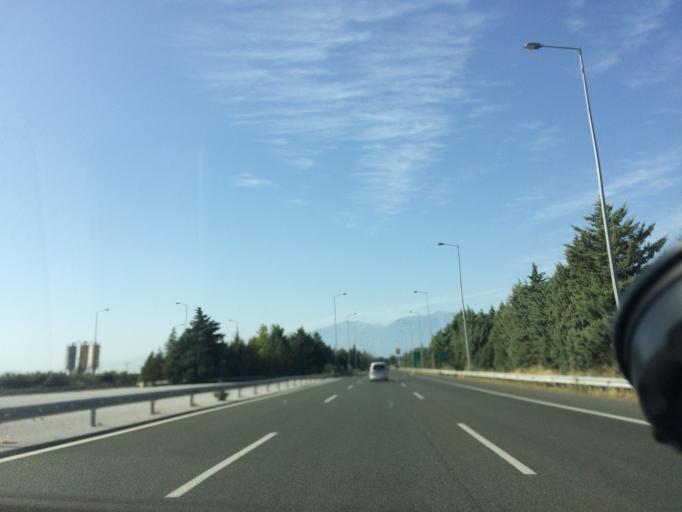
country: GR
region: Central Macedonia
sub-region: Nomos Pierias
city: Korinos
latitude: 40.3364
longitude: 22.5856
